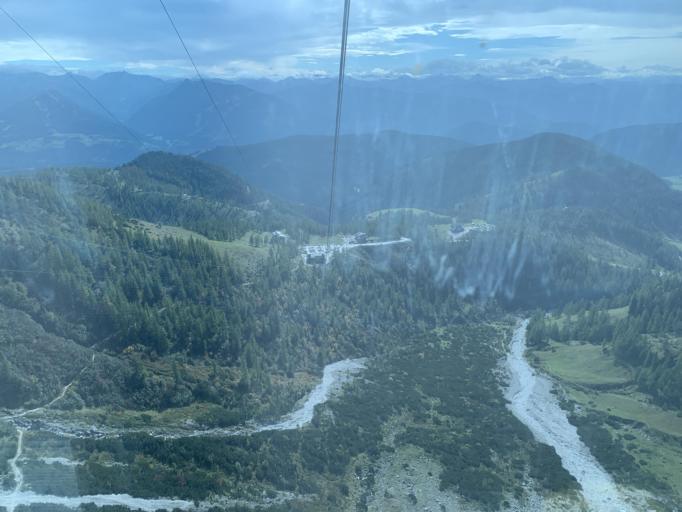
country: AT
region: Styria
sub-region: Politischer Bezirk Liezen
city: Schladming
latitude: 47.4581
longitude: 13.6214
